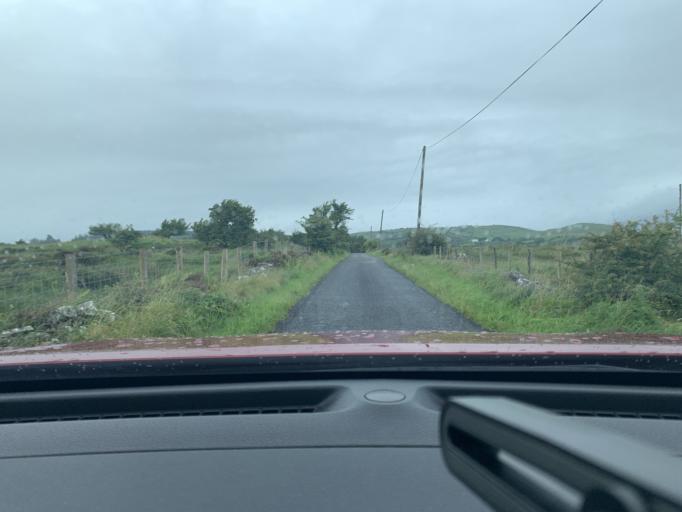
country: GB
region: Northern Ireland
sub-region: Fermanagh District
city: Enniskillen
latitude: 54.2569
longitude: -7.8420
